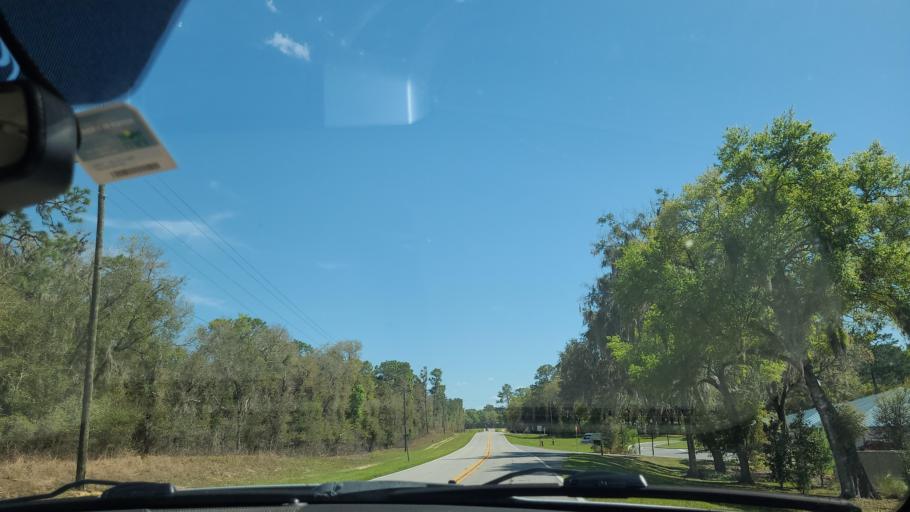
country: US
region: Florida
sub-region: Putnam County
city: Crescent City
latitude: 29.3640
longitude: -81.7391
